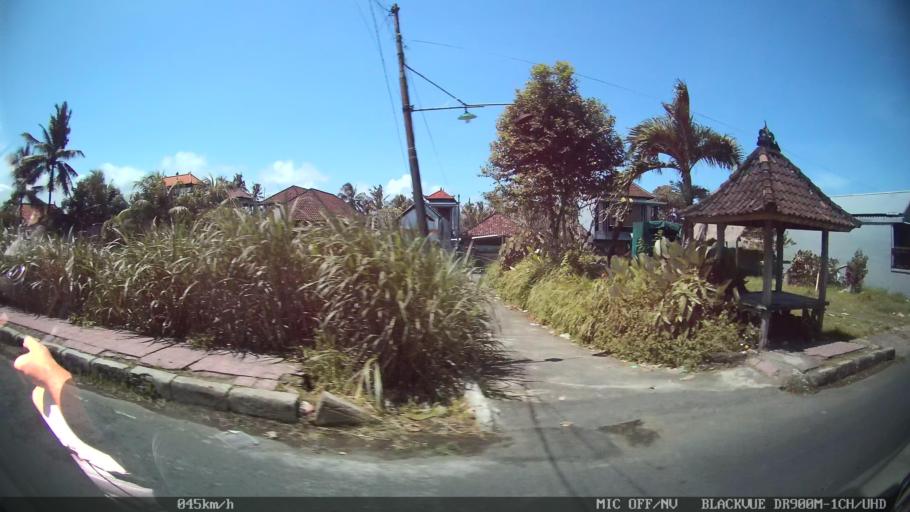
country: ID
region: Bali
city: Klungkung
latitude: -8.5700
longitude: 115.3479
